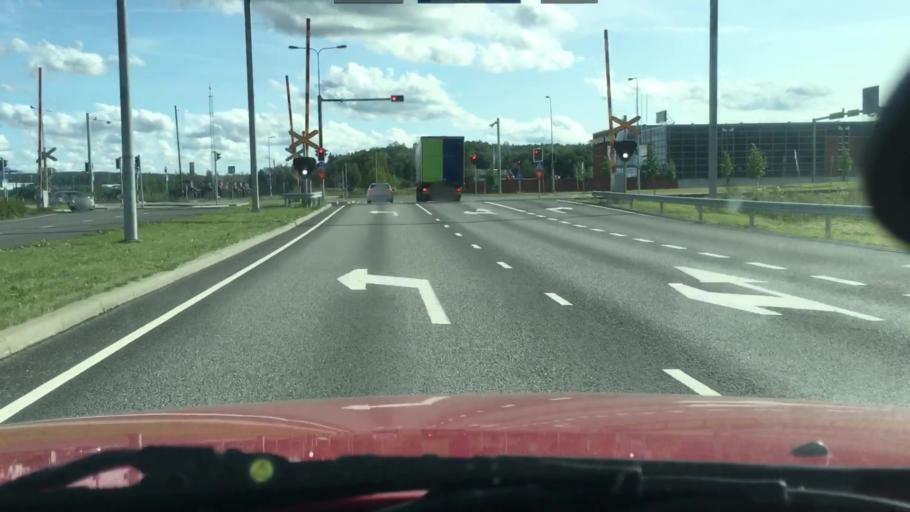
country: FI
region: Varsinais-Suomi
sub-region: Turku
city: Raisio
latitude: 60.4485
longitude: 22.2017
